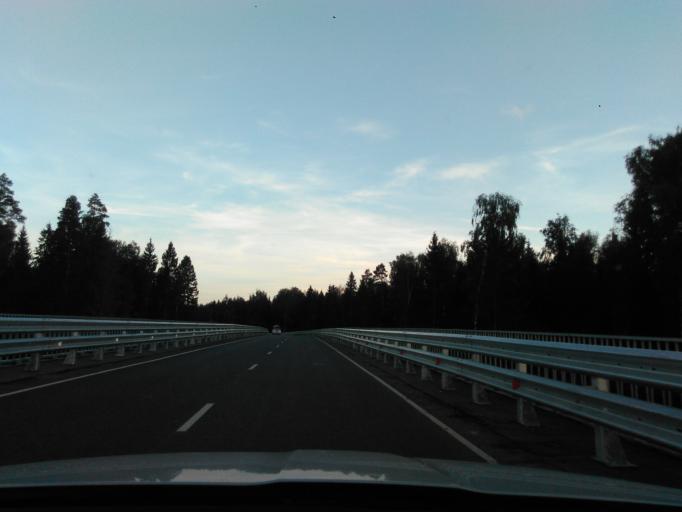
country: RU
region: Moskovskaya
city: Klin
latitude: 56.2085
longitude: 36.8090
